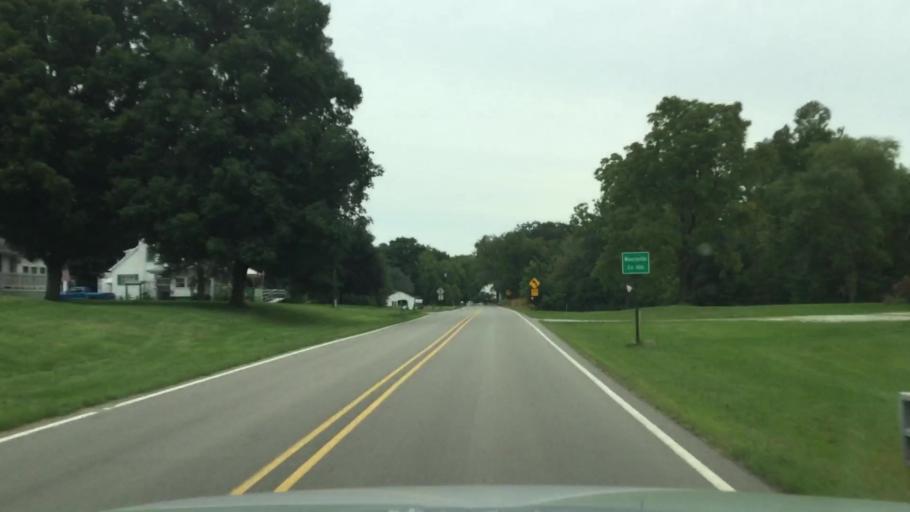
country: US
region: Michigan
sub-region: Washtenaw County
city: Milan
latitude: 42.0982
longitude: -83.7349
